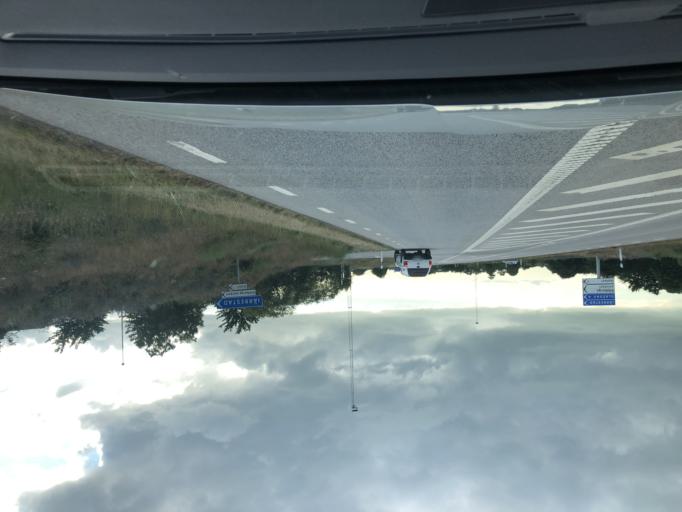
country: SE
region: Skane
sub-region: Simrishamns Kommun
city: Simrishamn
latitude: 55.5351
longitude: 14.2792
